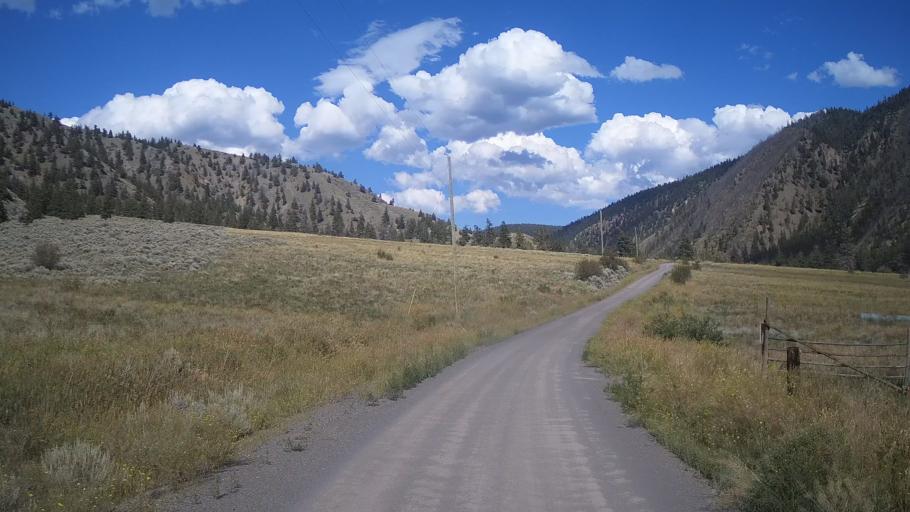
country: CA
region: British Columbia
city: Lillooet
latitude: 51.2217
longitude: -122.0877
